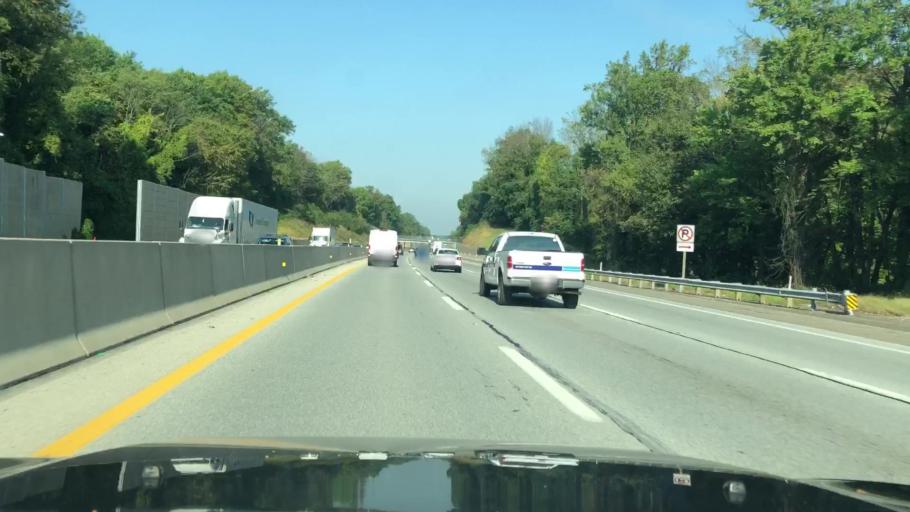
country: US
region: Pennsylvania
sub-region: Bucks County
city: Feasterville
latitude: 40.1535
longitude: -75.0300
